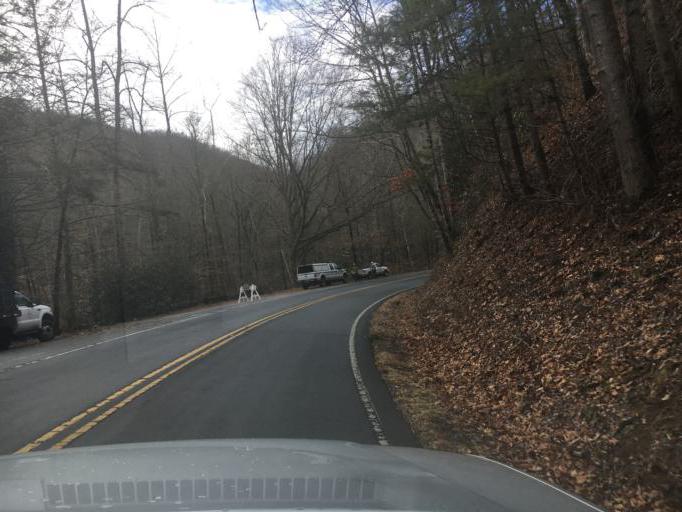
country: US
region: North Carolina
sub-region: Transylvania County
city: Brevard
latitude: 35.2810
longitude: -82.7525
